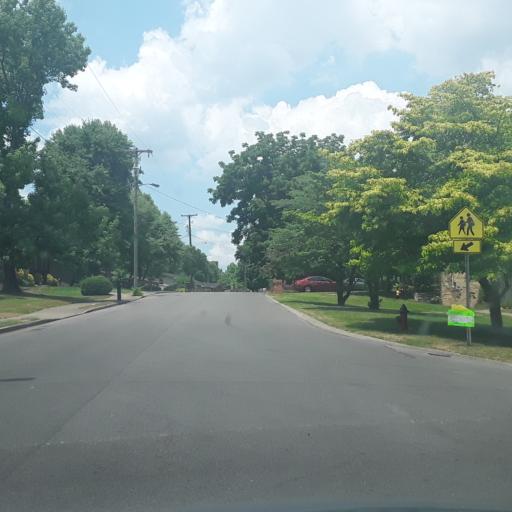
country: US
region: Tennessee
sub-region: Williamson County
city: Brentwood Estates
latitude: 36.0567
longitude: -86.6950
